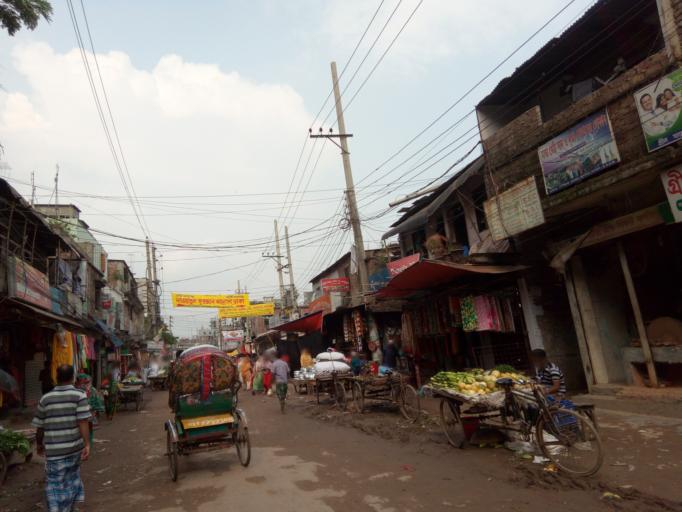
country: BD
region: Dhaka
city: Paltan
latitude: 23.7290
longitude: 90.4359
